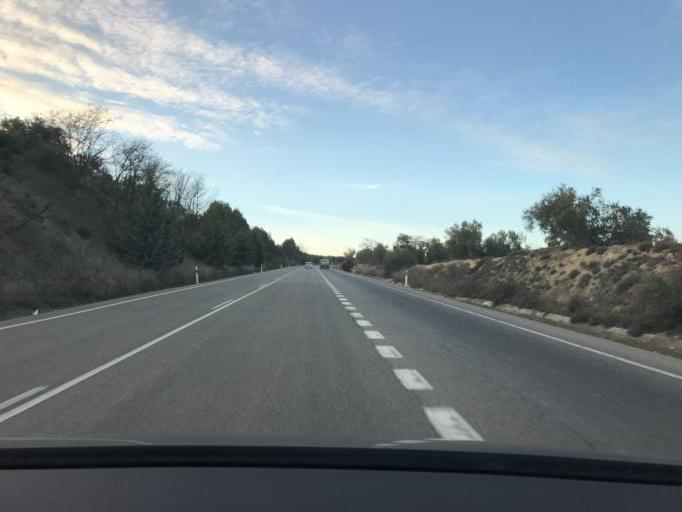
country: ES
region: Andalusia
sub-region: Provincia de Jaen
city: Ubeda
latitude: 37.9711
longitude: -3.3710
